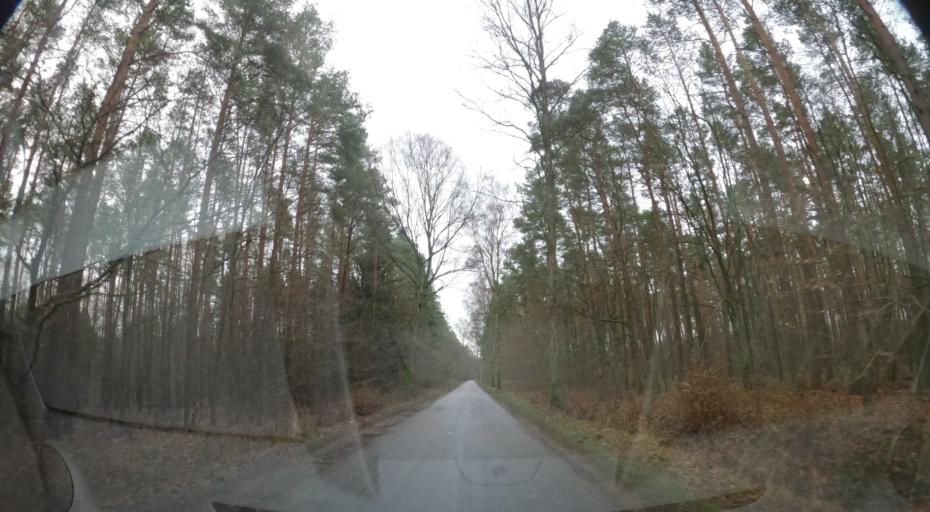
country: PL
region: Greater Poland Voivodeship
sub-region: Powiat zlotowski
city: Krajenka
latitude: 53.2861
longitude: 17.0662
